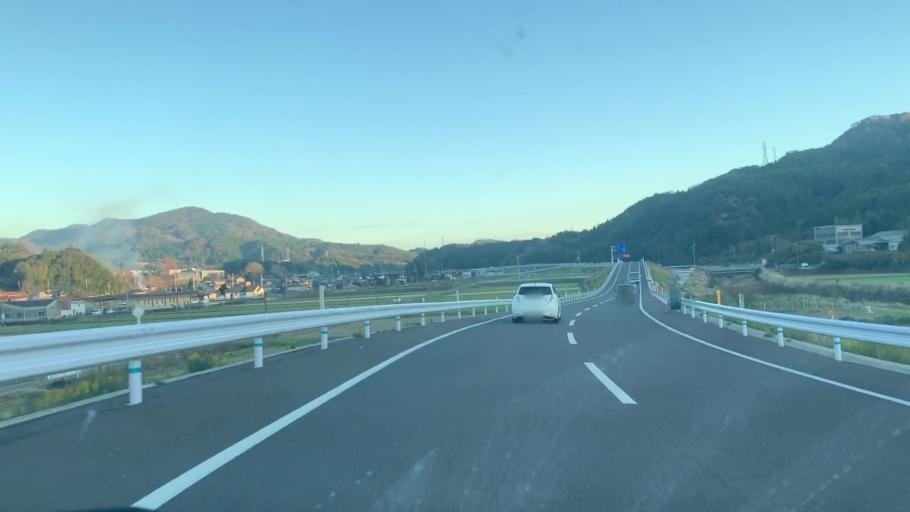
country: JP
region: Saga Prefecture
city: Takeocho-takeo
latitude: 33.2547
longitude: 129.9873
